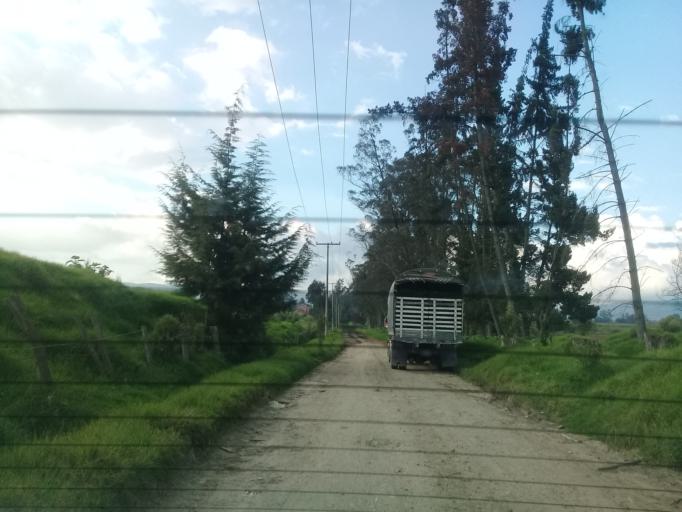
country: CO
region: Cundinamarca
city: Madrid
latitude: 4.7871
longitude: -74.2742
